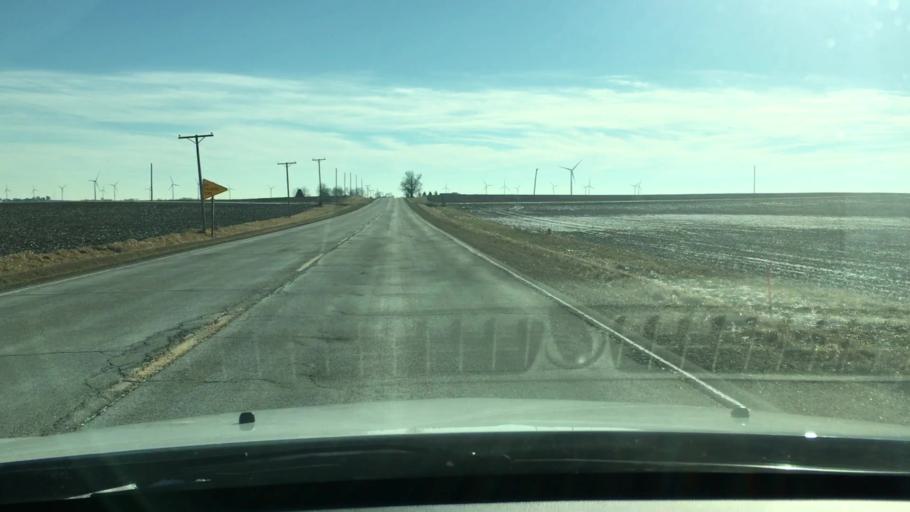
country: US
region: Illinois
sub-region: LaSalle County
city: Mendota
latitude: 41.6733
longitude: -89.1297
